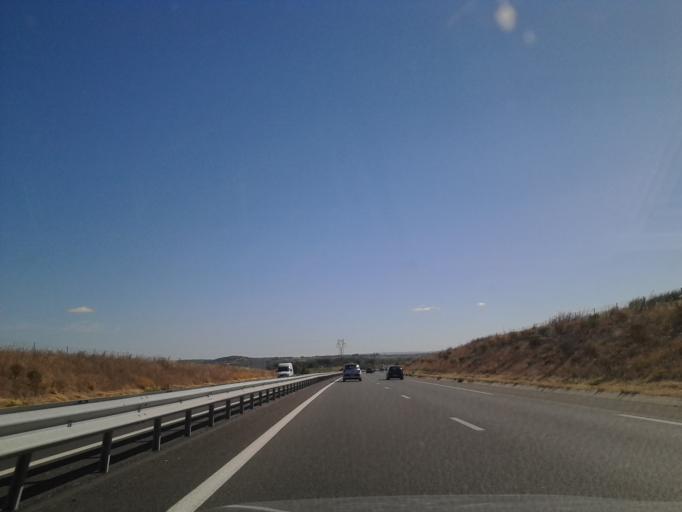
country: FR
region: Languedoc-Roussillon
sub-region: Departement de l'Herault
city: Servian
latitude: 43.3914
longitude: 3.3211
